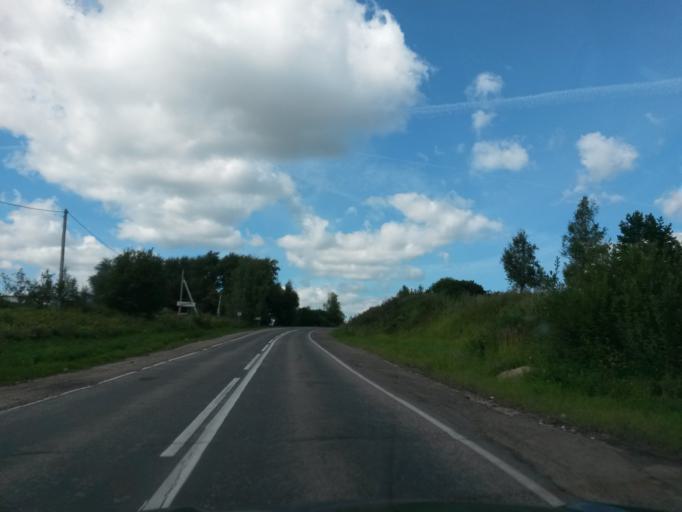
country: RU
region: Jaroslavl
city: Yaroslavl
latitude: 57.5420
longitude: 39.8637
